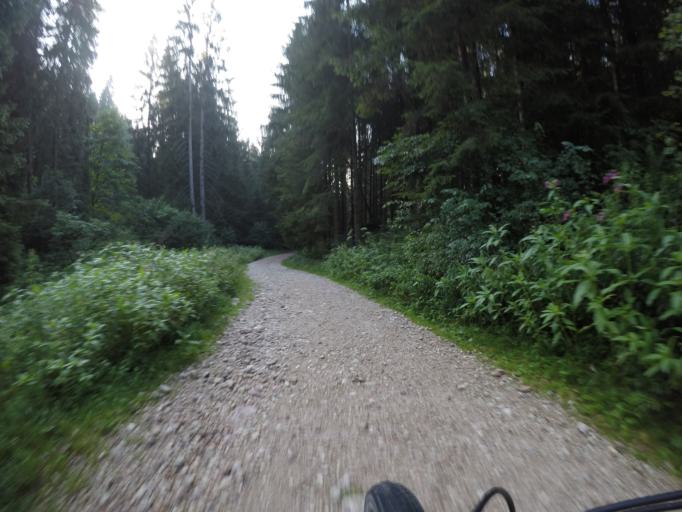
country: IT
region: Veneto
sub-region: Provincia di Vicenza
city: Asiago
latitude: 45.8541
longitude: 11.5144
